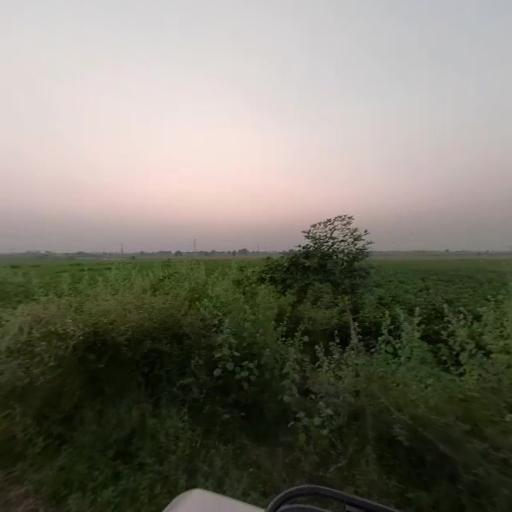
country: IN
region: Telangana
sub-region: Nalgonda
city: Suriapet
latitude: 17.1112
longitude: 79.5287
